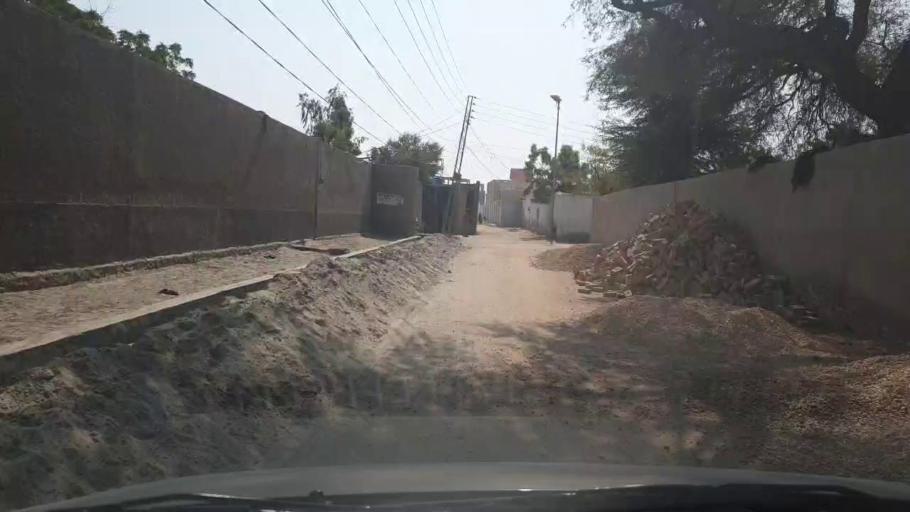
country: PK
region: Sindh
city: Mirwah Gorchani
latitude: 25.3116
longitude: 69.1548
